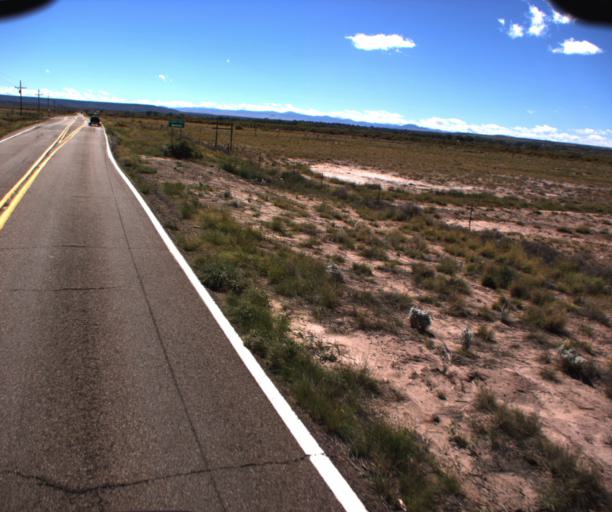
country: US
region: Arizona
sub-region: Apache County
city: Saint Johns
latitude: 34.5338
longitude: -109.3454
